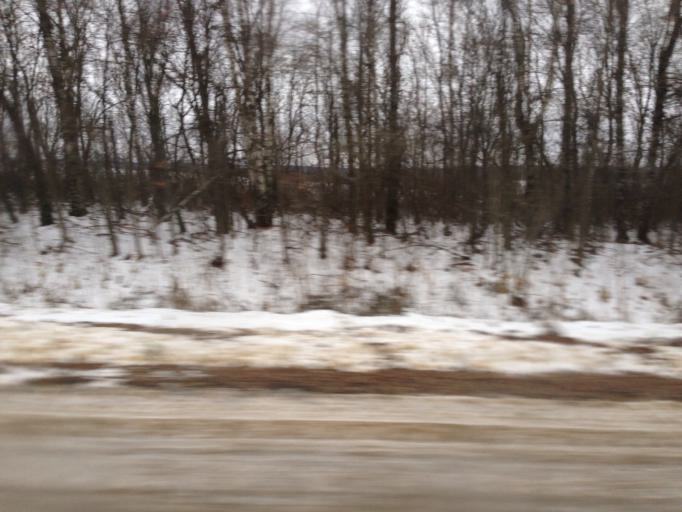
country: RU
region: Tula
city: Bolokhovo
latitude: 54.0462
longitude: 37.8521
